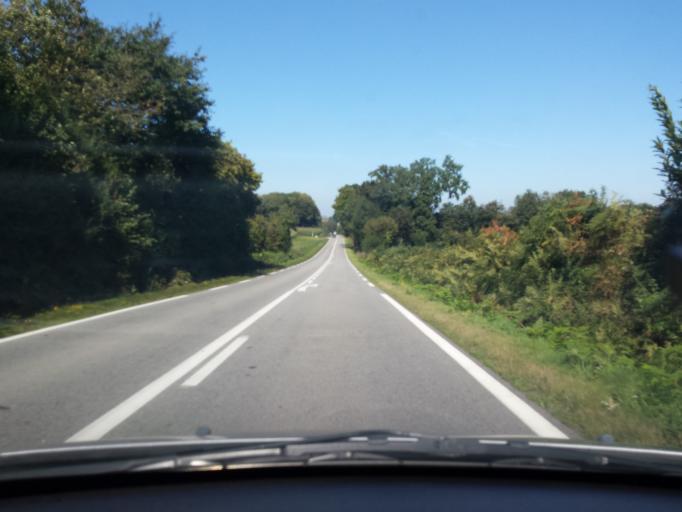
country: FR
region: Brittany
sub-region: Departement du Morbihan
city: Saint-Thuriau
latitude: 48.0332
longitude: -2.9200
